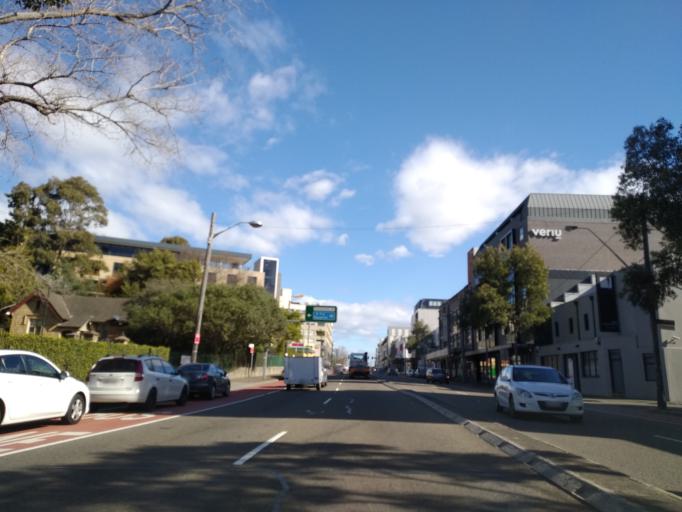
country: AU
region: New South Wales
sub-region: Marrickville
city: Camperdown
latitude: -33.8857
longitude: 151.1813
